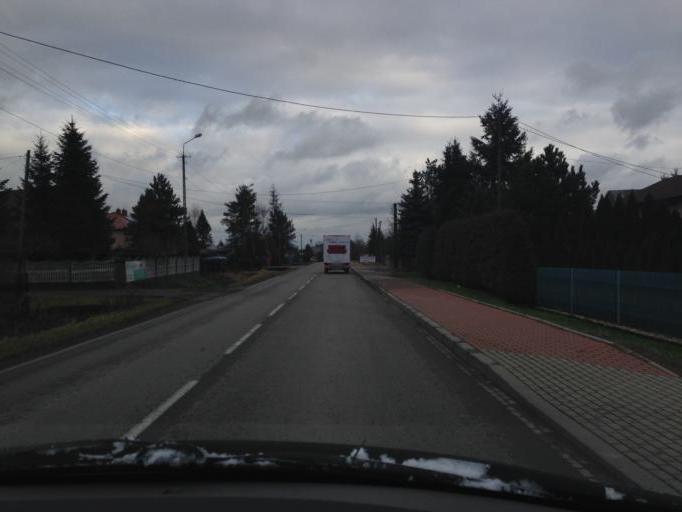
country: PL
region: Lesser Poland Voivodeship
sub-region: Powiat wielicki
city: Gdow
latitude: 49.9080
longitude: 20.1850
